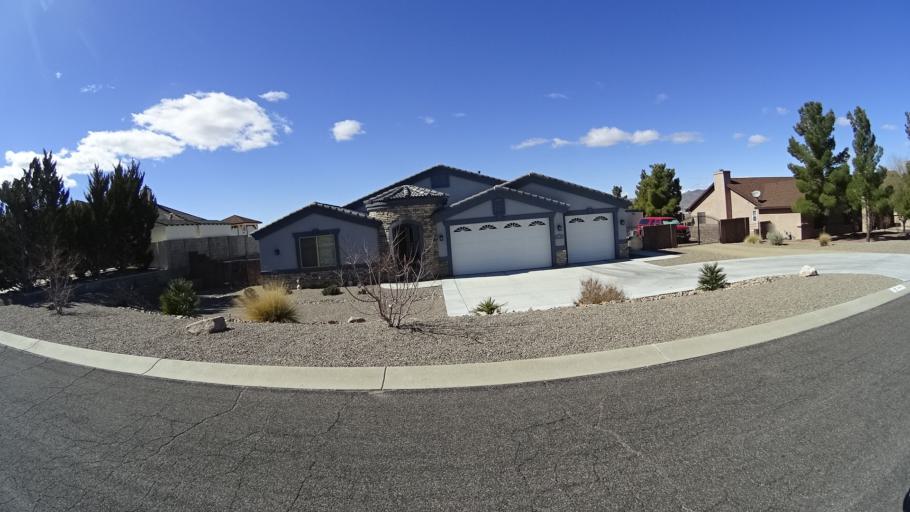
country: US
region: Arizona
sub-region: Mohave County
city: Kingman
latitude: 35.2006
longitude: -113.9754
